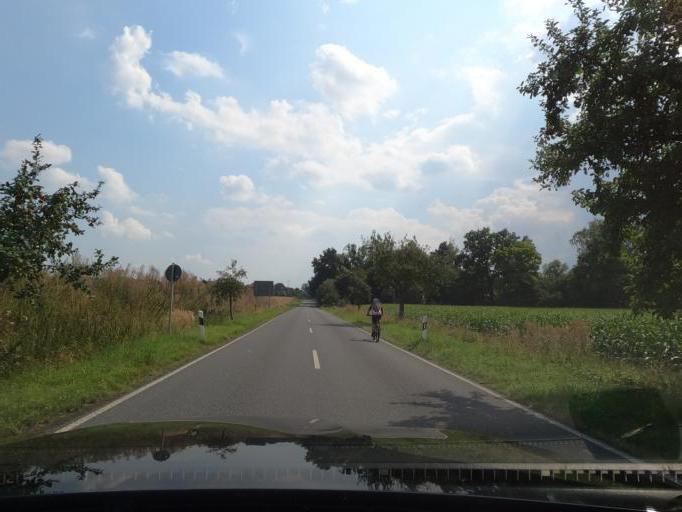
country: DE
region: Lower Saxony
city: Alt Wallmoden
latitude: 52.0269
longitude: 10.3431
